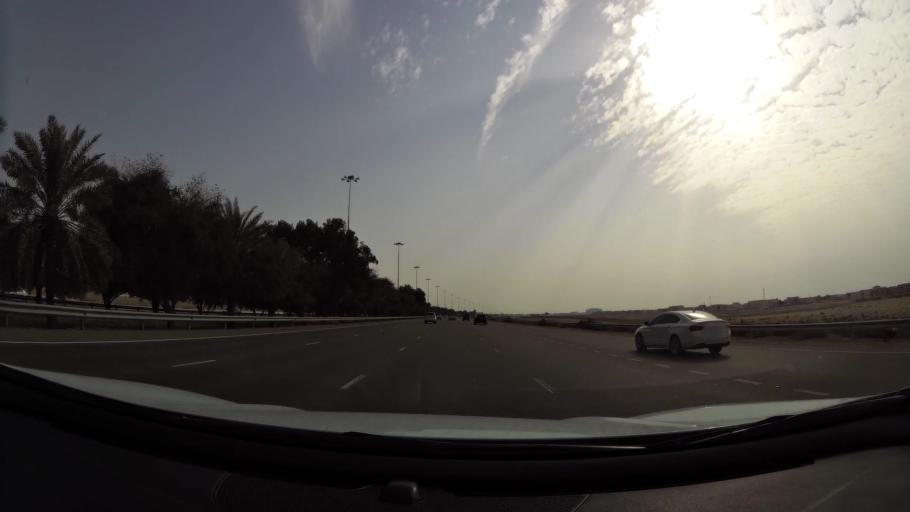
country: AE
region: Abu Dhabi
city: Abu Dhabi
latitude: 24.3666
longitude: 54.6529
